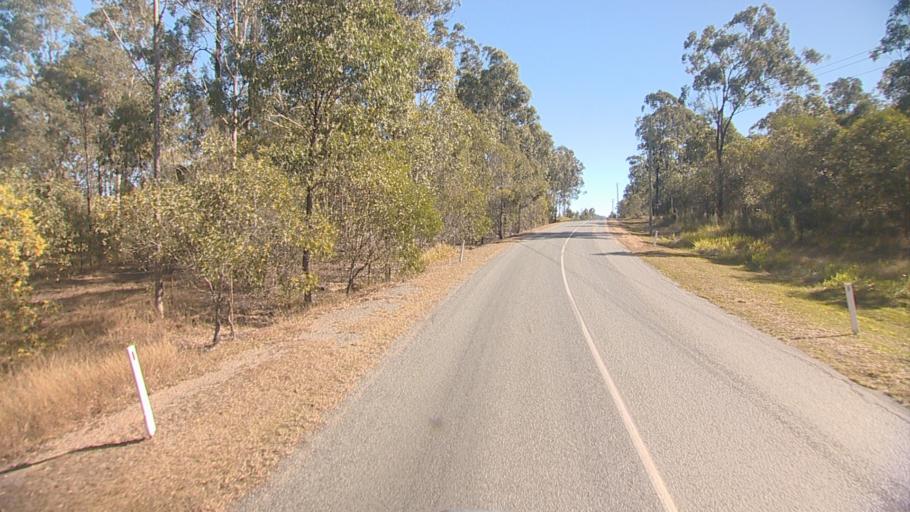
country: AU
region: Queensland
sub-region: Ipswich
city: Springfield Lakes
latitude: -27.7317
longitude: 152.9397
